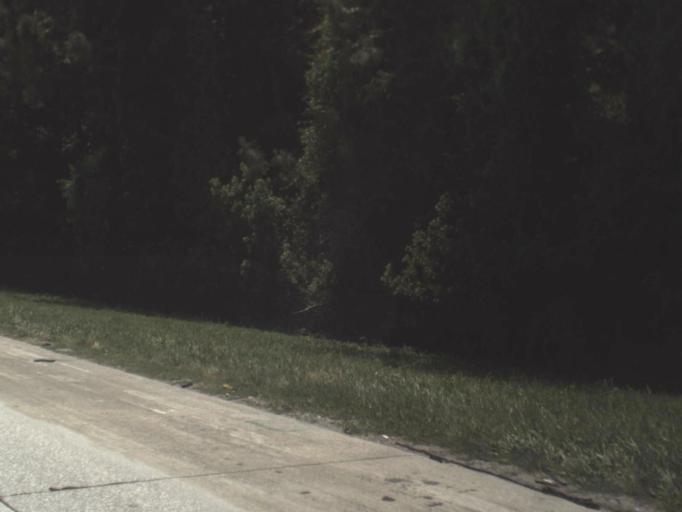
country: US
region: Florida
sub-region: Duval County
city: Jacksonville
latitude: 30.2417
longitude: -81.5865
